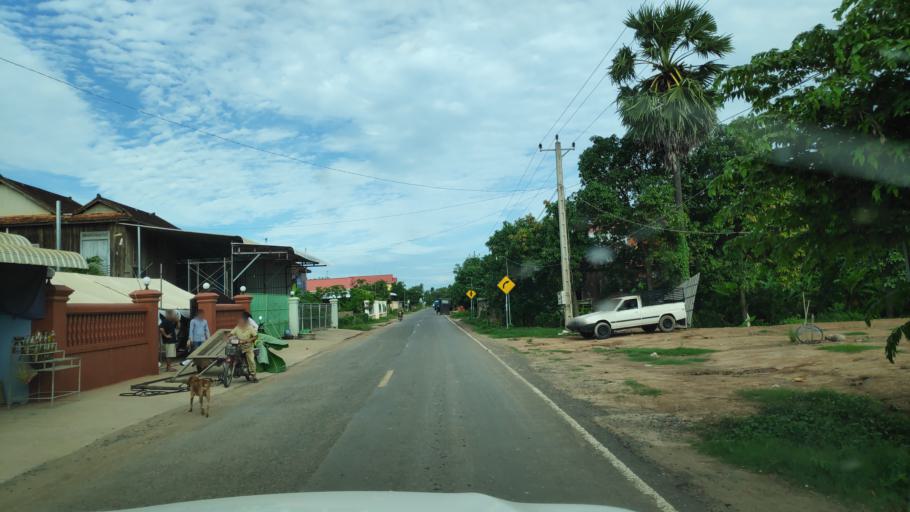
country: KH
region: Kampong Cham
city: Kampong Cham
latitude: 11.9467
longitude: 105.2463
